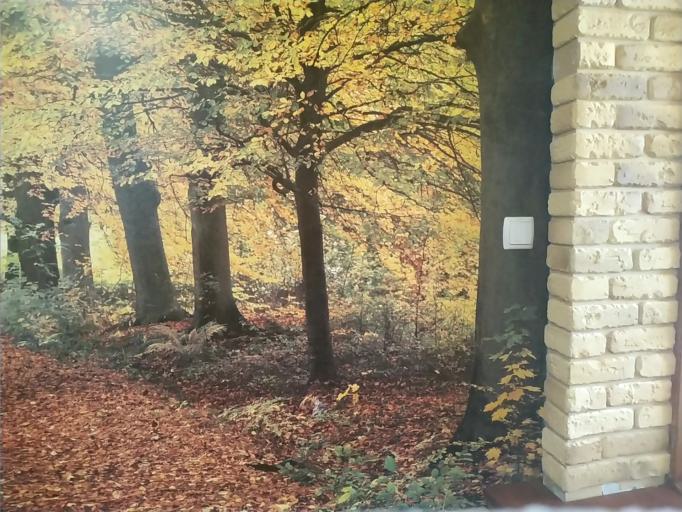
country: RU
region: Tverskaya
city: Vyshniy Volochek
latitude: 57.6333
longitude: 34.5712
